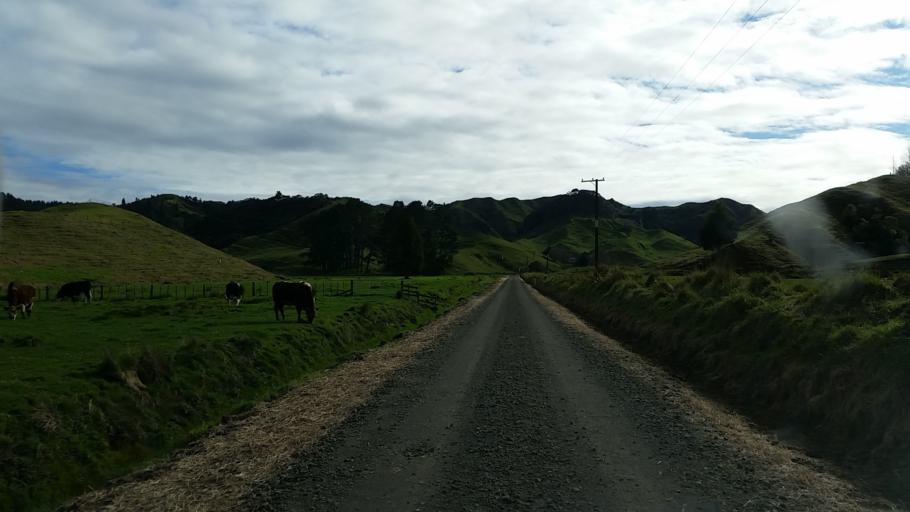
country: NZ
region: Taranaki
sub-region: South Taranaki District
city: Eltham
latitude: -39.2290
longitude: 174.5650
